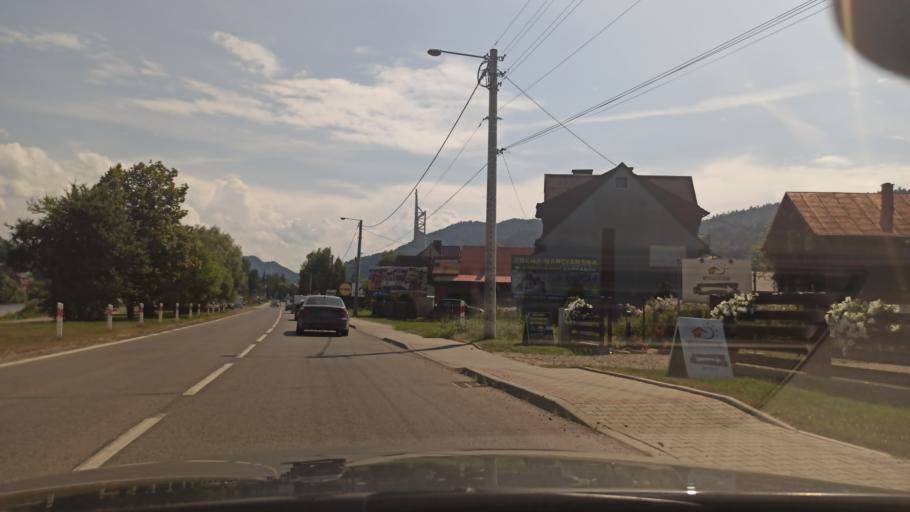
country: PL
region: Lesser Poland Voivodeship
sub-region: Powiat nowotarski
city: Kroscienko nad Dunajcem
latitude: 49.4454
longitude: 20.4245
